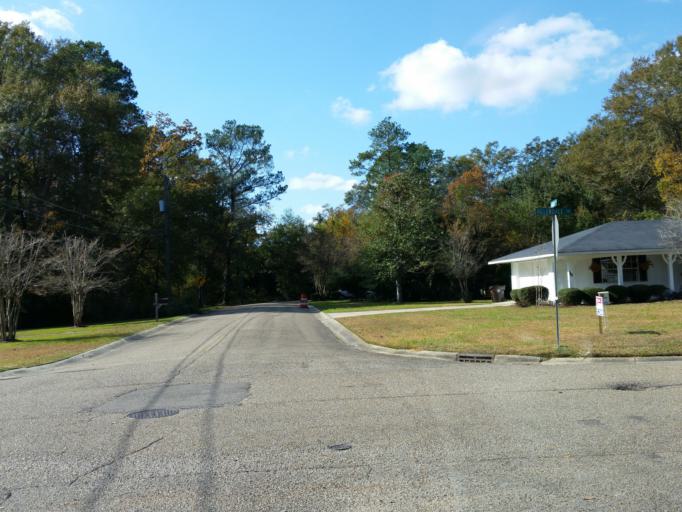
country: US
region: Mississippi
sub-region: Lamar County
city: West Hattiesburg
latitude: 31.3071
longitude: -89.3338
